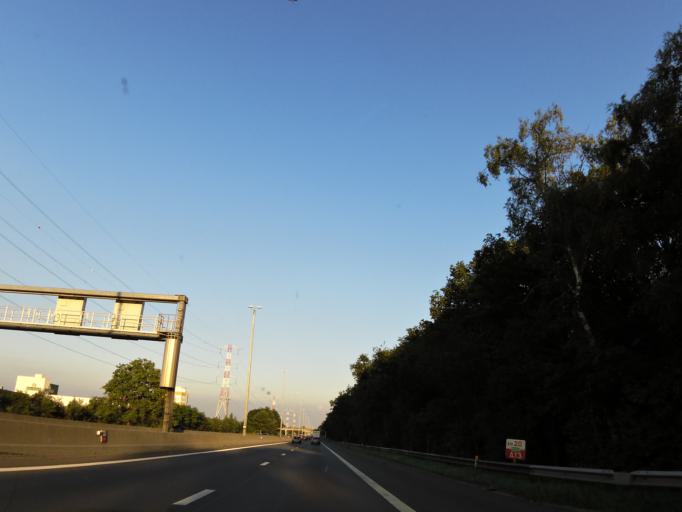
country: BE
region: Flanders
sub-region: Provincie Antwerpen
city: Grobbendonk
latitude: 51.1790
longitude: 4.7223
